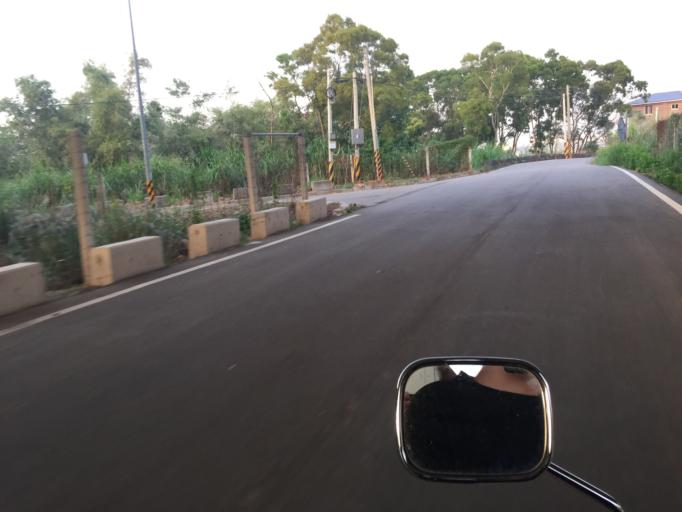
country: TW
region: Taiwan
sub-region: Miaoli
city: Miaoli
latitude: 24.4727
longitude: 120.7735
